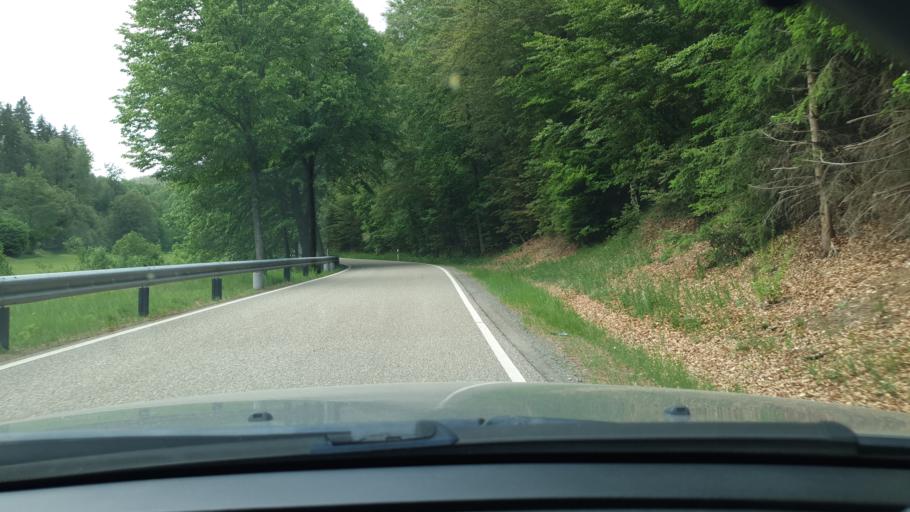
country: DE
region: Rheinland-Pfalz
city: Trippstadt
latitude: 49.3853
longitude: 7.8001
